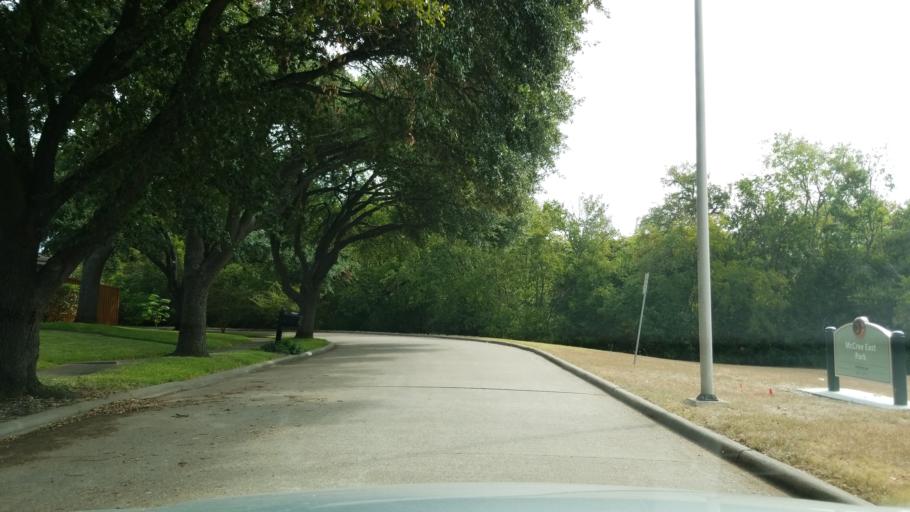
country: US
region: Texas
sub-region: Dallas County
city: Garland
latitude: 32.8738
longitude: -96.6920
